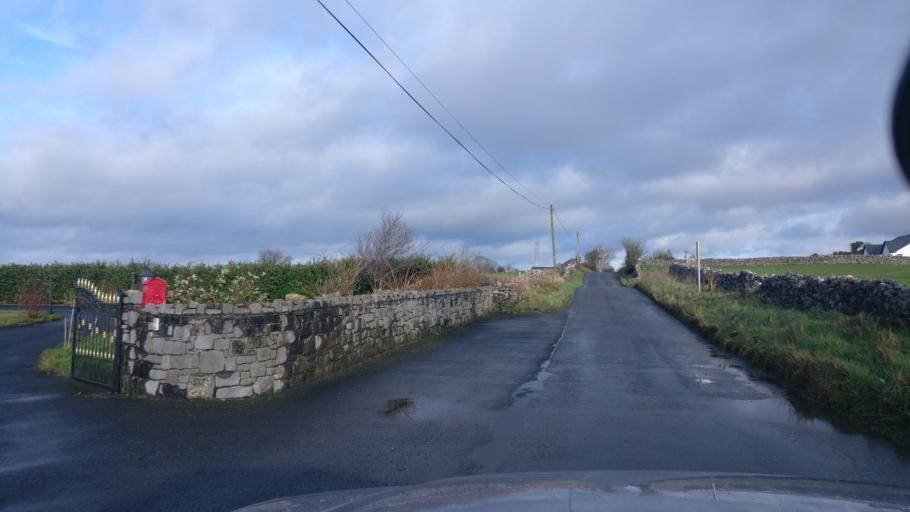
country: IE
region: Connaught
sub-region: County Galway
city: Loughrea
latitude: 53.2132
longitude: -8.5470
